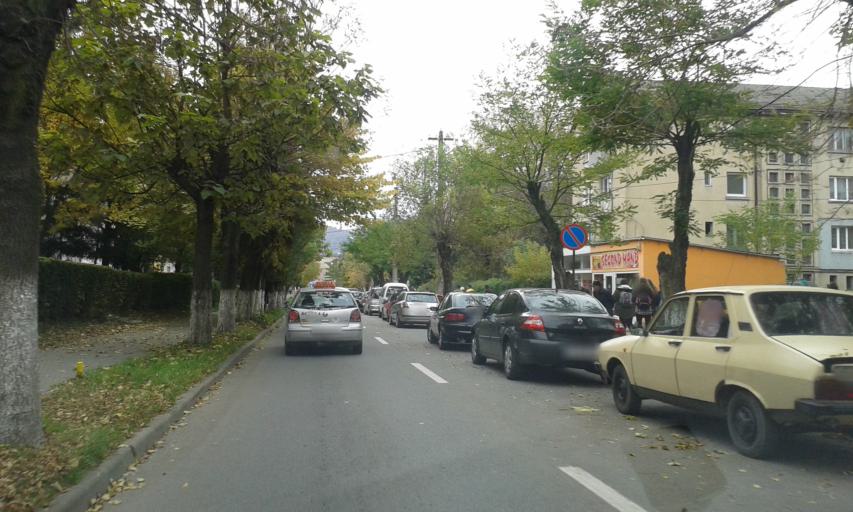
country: RO
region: Hunedoara
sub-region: Municipiul Petrosani
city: Petrosani
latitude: 45.4003
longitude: 23.3744
